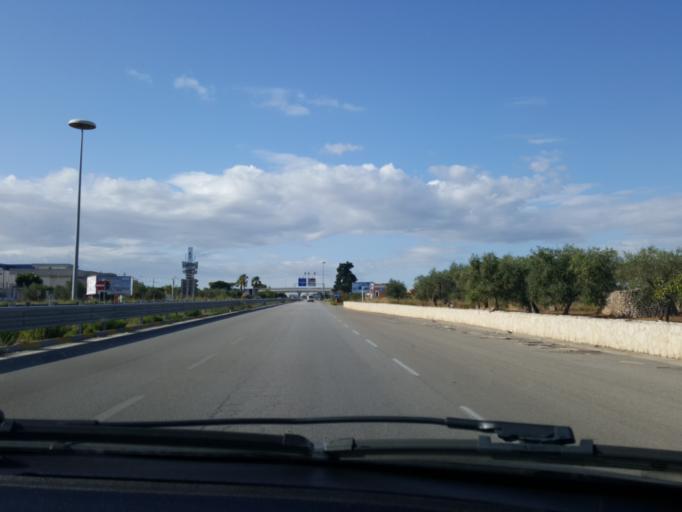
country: IT
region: Apulia
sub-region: Provincia di Bari
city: Triggiano
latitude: 41.0869
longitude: 16.9476
